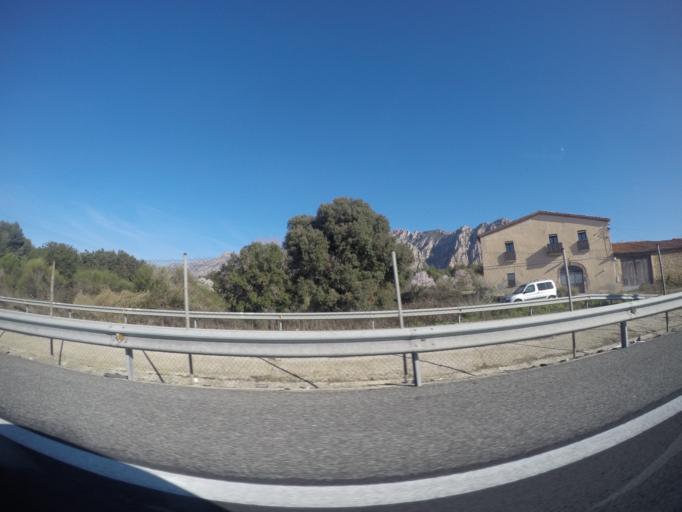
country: ES
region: Catalonia
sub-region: Provincia de Barcelona
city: Collbato
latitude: 41.5627
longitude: 1.8250
